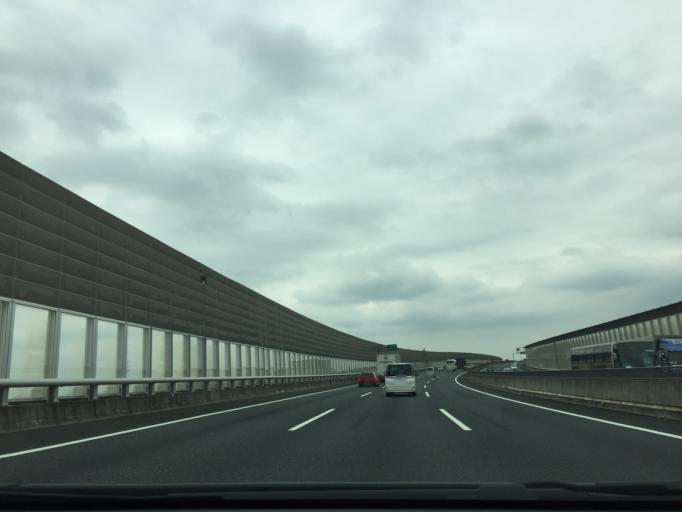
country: JP
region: Aichi
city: Obu
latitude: 35.0426
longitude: 136.9811
